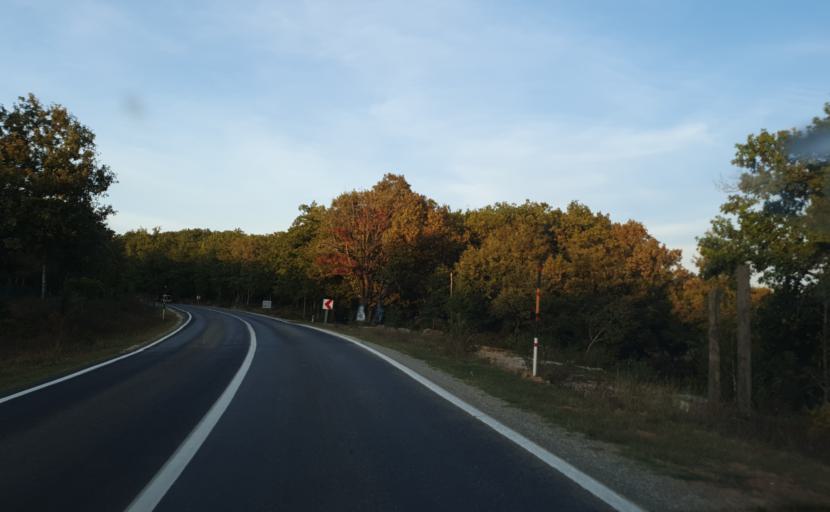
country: TR
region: Kirklareli
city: Sergen
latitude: 41.8413
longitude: 27.8040
